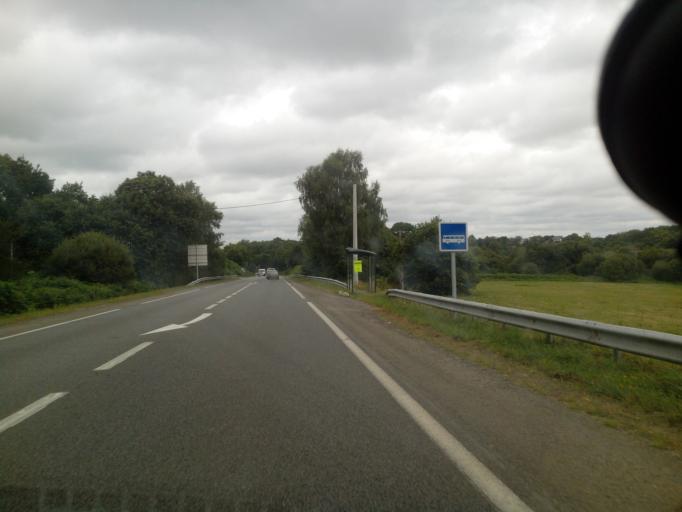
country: FR
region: Brittany
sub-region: Departement du Morbihan
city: Hennebont
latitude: 47.7747
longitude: -3.2748
